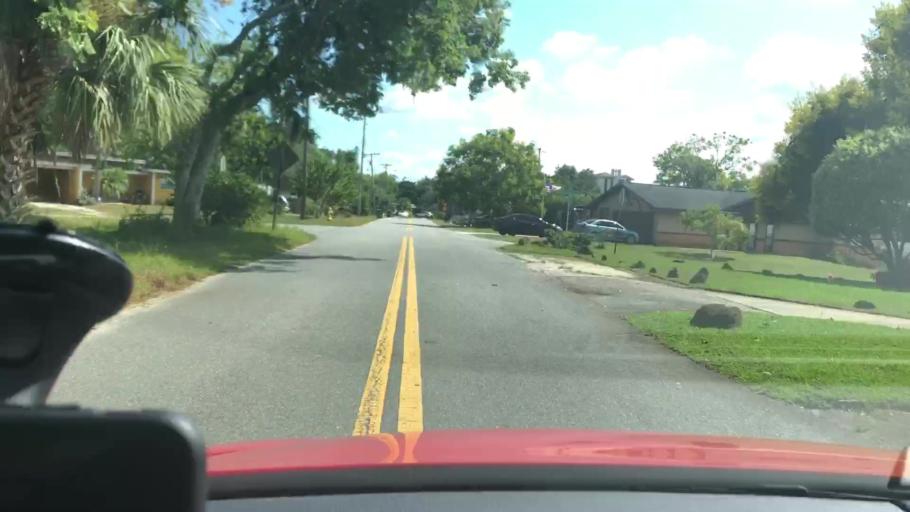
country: US
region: Florida
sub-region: Volusia County
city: Daytona Beach
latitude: 29.2095
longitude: -81.0564
